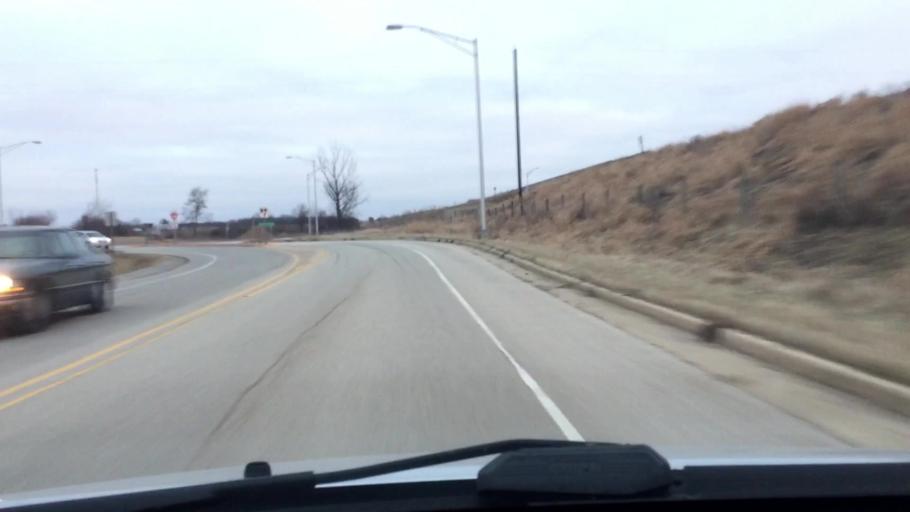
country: US
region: Wisconsin
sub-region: Jefferson County
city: Watertown
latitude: 43.1585
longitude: -88.7498
